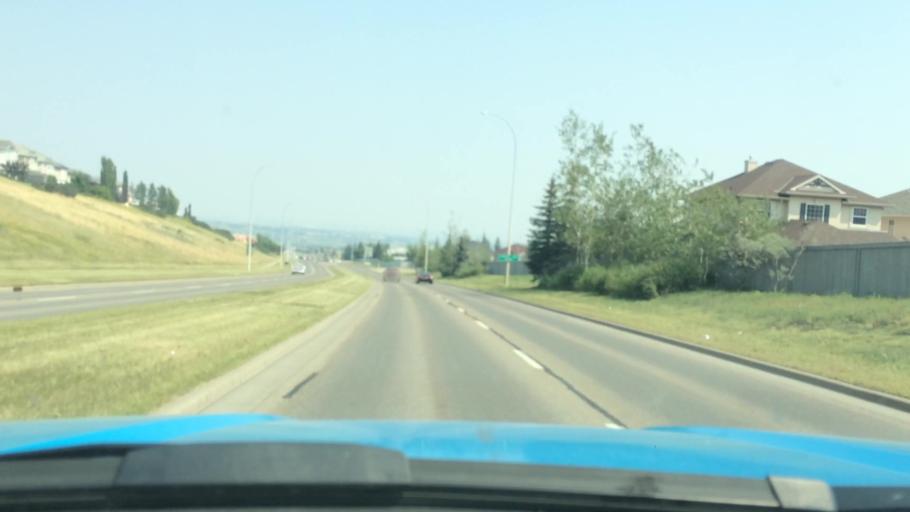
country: CA
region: Alberta
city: Calgary
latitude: 51.1389
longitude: -114.1387
